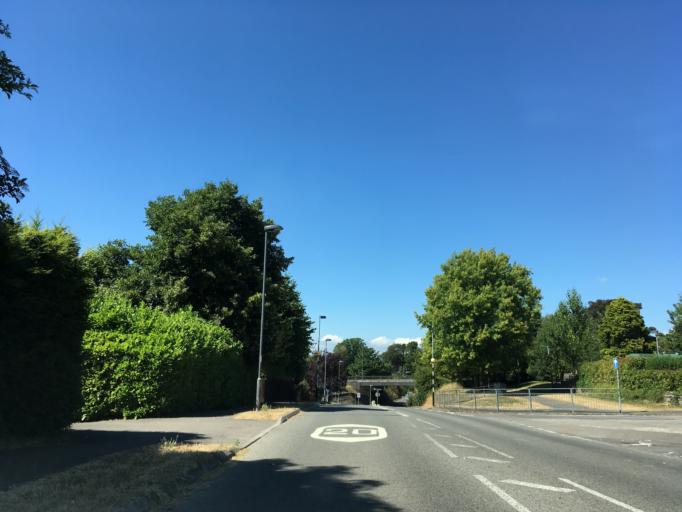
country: GB
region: England
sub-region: South Gloucestershire
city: Chipping Sodbury
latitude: 51.5335
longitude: -2.3965
